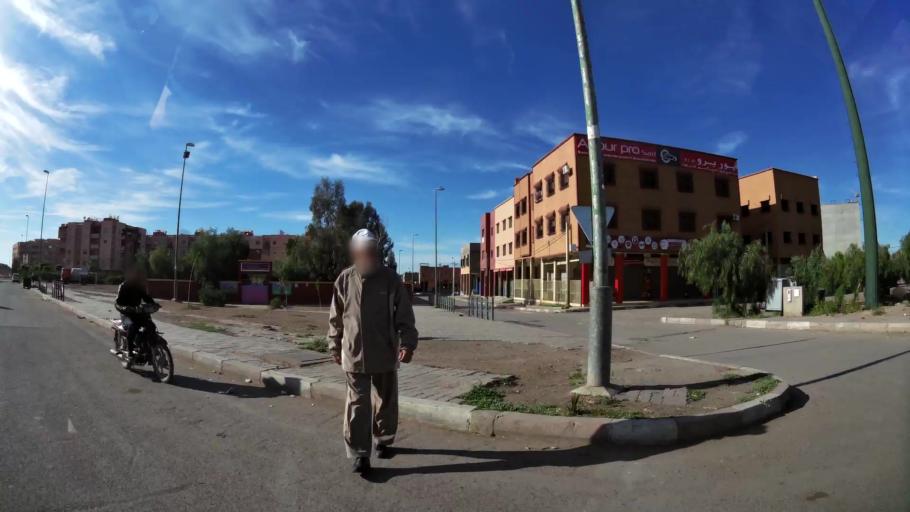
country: MA
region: Marrakech-Tensift-Al Haouz
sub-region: Marrakech
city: Marrakesh
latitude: 31.6853
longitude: -8.0621
